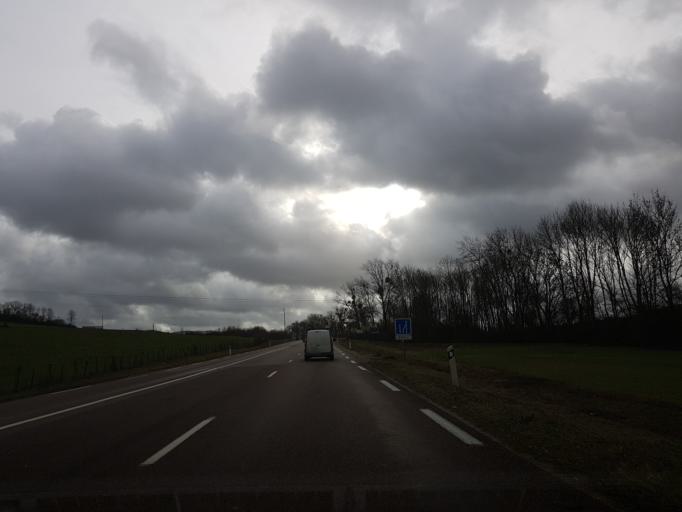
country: FR
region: Champagne-Ardenne
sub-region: Departement de la Haute-Marne
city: Langres
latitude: 47.8793
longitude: 5.3210
